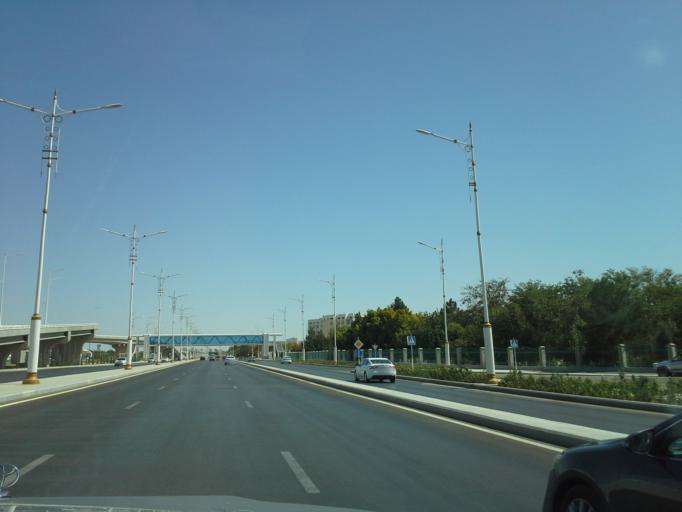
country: TM
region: Ahal
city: Ashgabat
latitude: 37.9265
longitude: 58.4297
